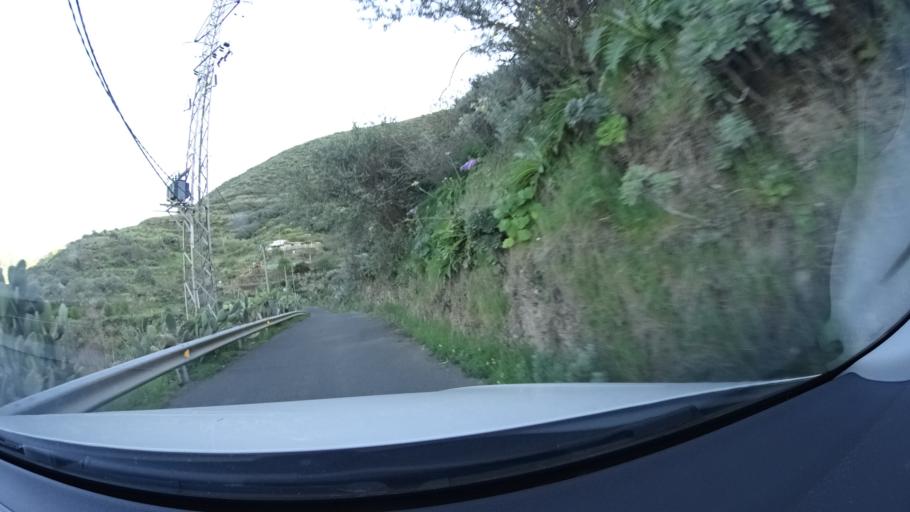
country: ES
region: Canary Islands
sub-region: Provincia de Las Palmas
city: Artenara
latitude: 28.0345
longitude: -15.6471
